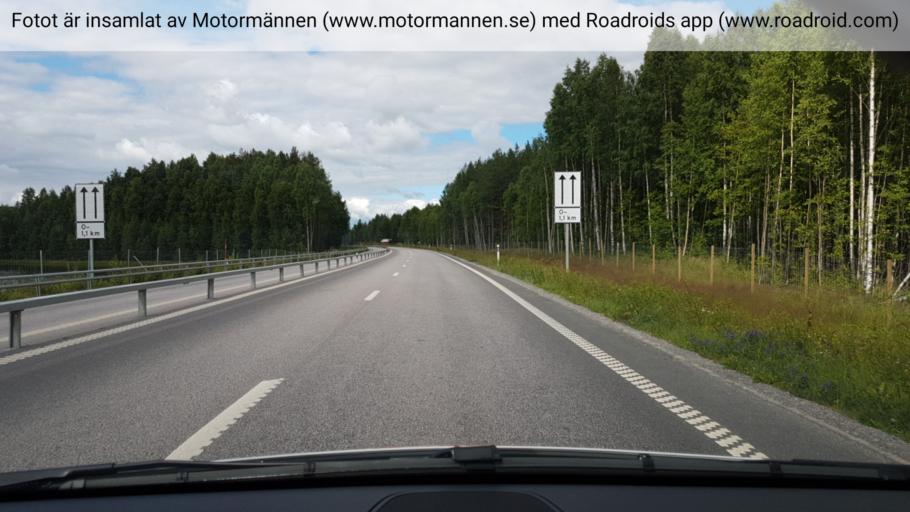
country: SE
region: Norrbotten
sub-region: Pitea Kommun
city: Bergsviken
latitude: 65.3141
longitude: 21.3978
